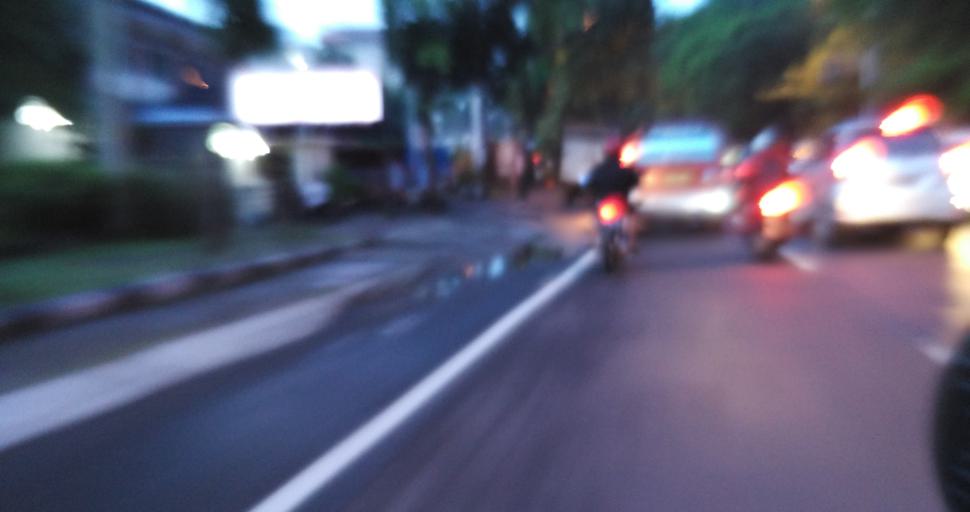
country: ID
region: Central Java
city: Semarang
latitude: -7.0100
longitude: 110.4158
